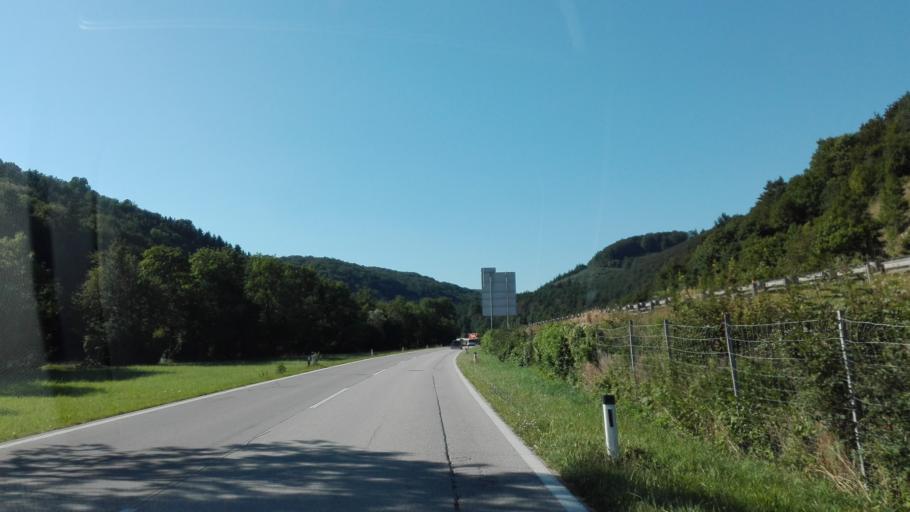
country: AT
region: Lower Austria
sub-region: Politischer Bezirk Baden
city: Alland
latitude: 48.0762
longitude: 16.0529
